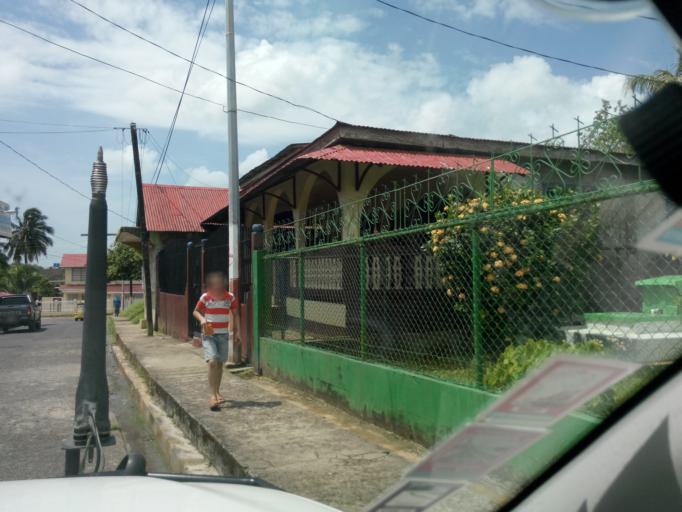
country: NI
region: Atlantico Sur
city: Bluefields
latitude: 12.0146
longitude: -83.7615
